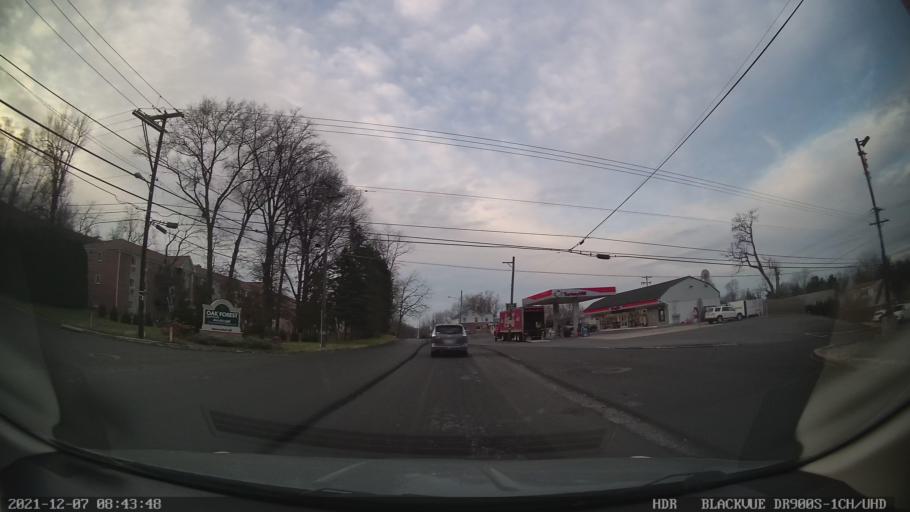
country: US
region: Pennsylvania
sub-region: Berks County
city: Laureldale
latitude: 40.3692
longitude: -75.8999
